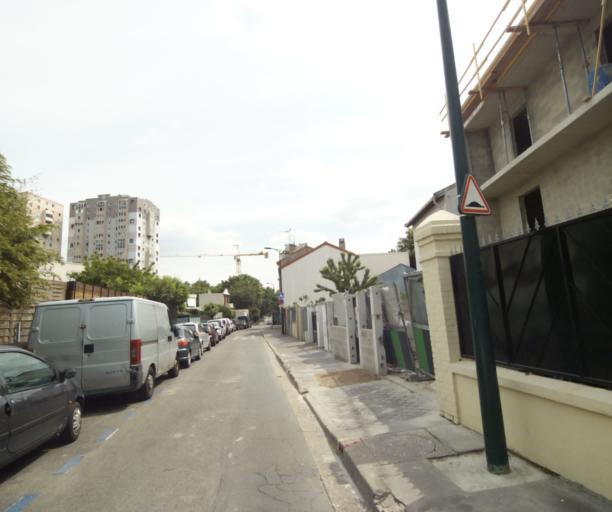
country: FR
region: Ile-de-France
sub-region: Departement des Hauts-de-Seine
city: Bois-Colombes
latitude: 48.9303
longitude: 2.2699
